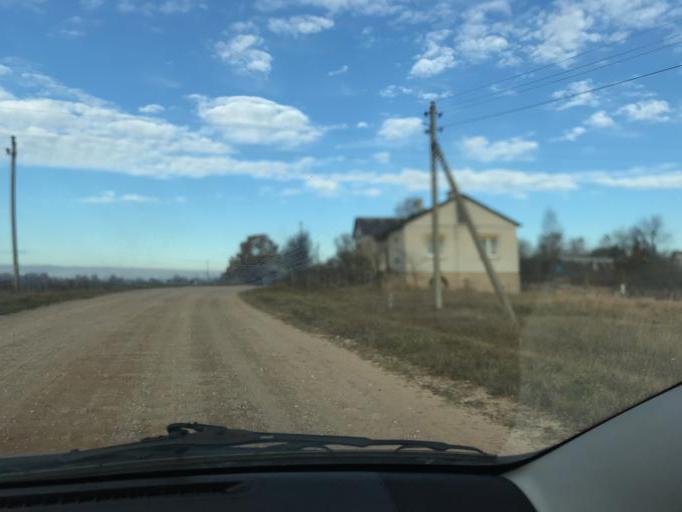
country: BY
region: Vitebsk
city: Haradok
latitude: 55.4558
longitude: 30.0126
